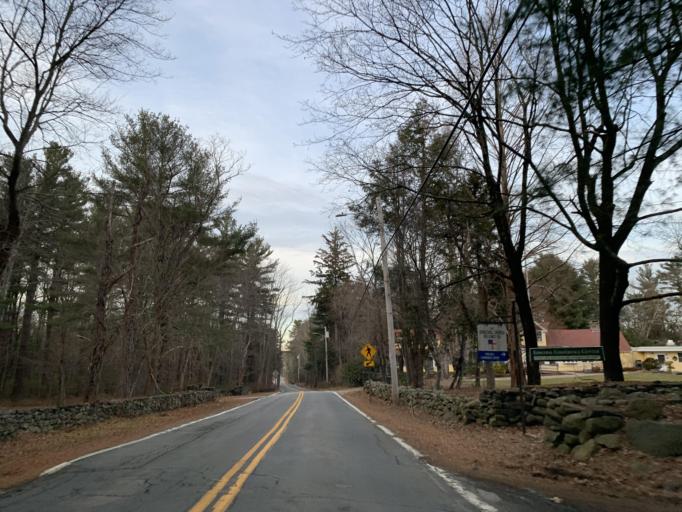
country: US
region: Rhode Island
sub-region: Providence County
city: Pascoag
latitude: 41.9307
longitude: -71.7004
